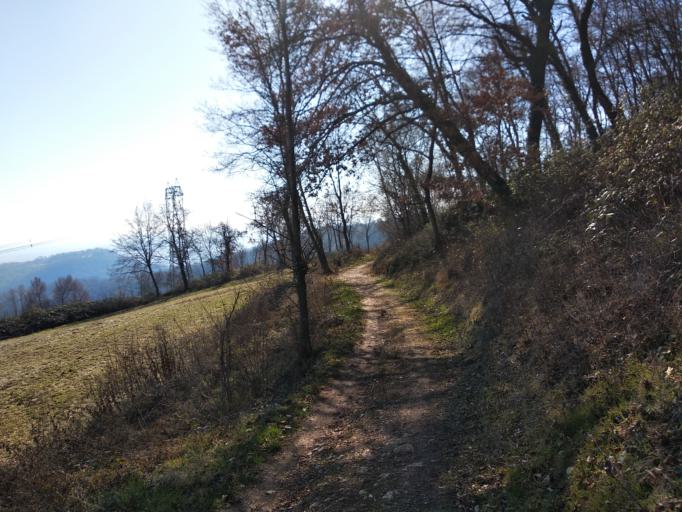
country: IT
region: Veneto
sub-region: Provincia di Vicenza
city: Gambugliano
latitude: 45.5912
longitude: 11.4558
